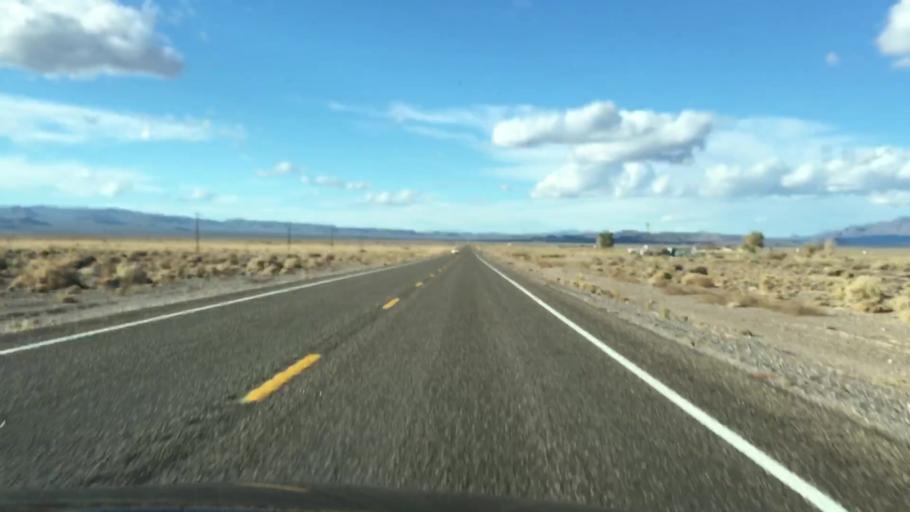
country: US
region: Nevada
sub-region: Nye County
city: Beatty
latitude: 37.2480
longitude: -117.0018
